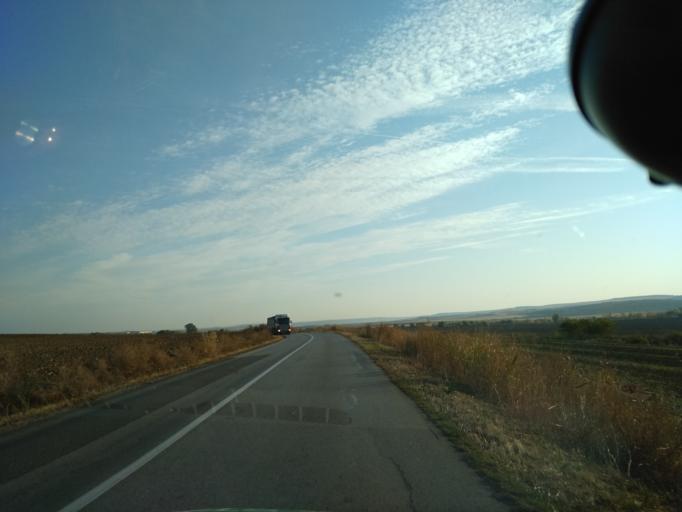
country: RO
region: Timis
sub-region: Comuna Fibis
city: Fibis
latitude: 45.9361
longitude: 21.3974
